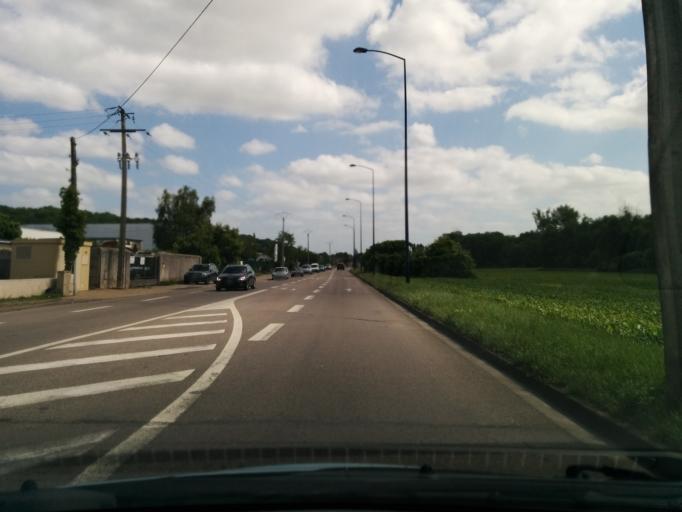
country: FR
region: Ile-de-France
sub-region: Departement des Yvelines
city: Epone
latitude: 48.9561
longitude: 1.8303
